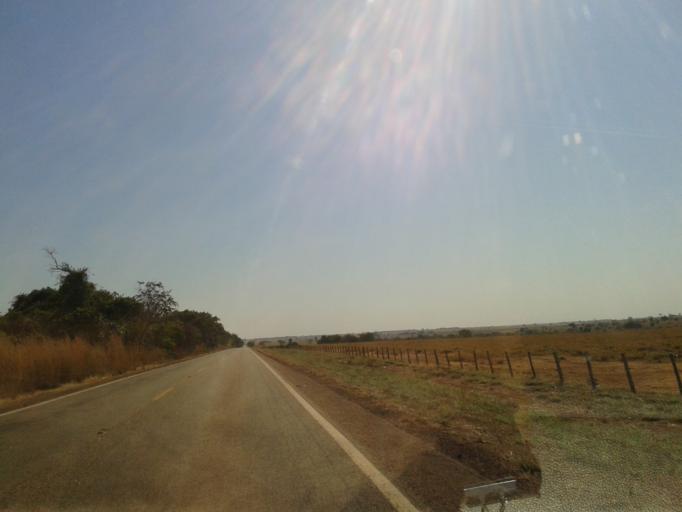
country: BR
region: Goias
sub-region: Mozarlandia
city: Mozarlandia
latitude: -14.3863
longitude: -50.4368
